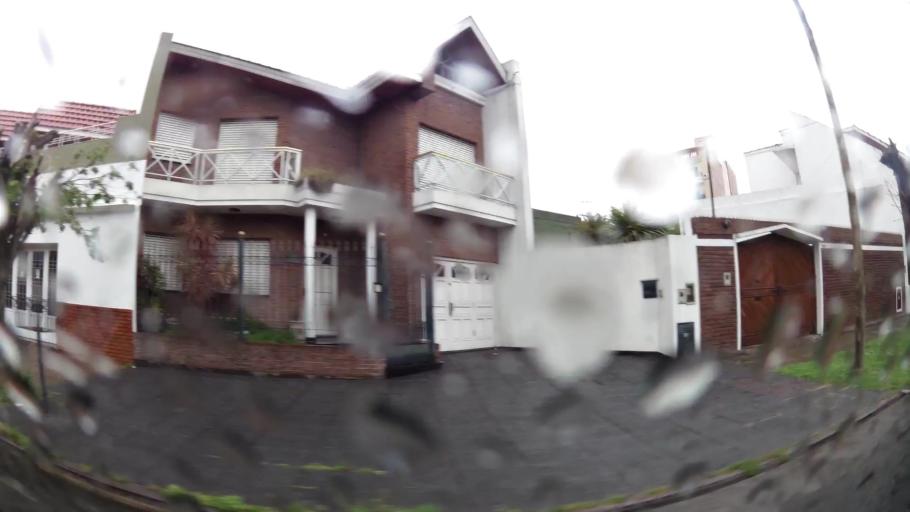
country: AR
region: Buenos Aires
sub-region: Partido de Lanus
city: Lanus
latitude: -34.7044
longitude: -58.4035
